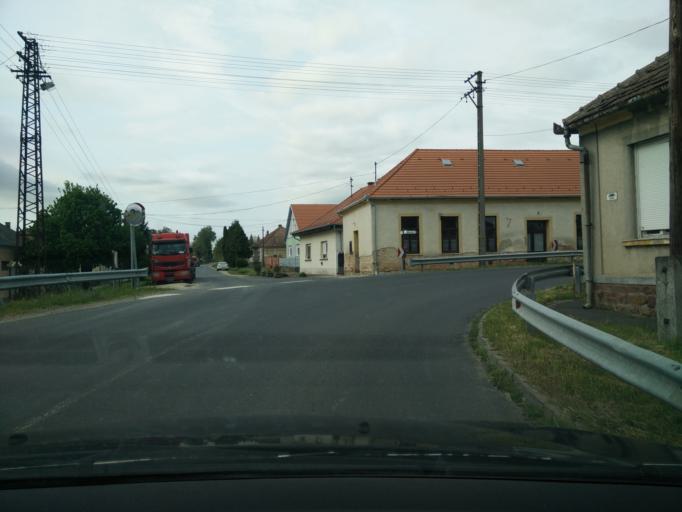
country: HU
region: Zala
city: Zalaszentgrot
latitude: 46.9895
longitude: 17.0358
